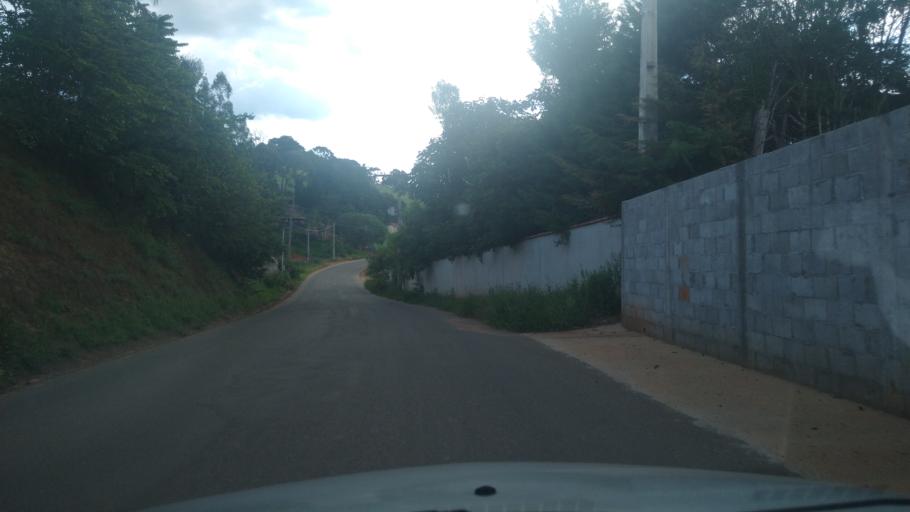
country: BR
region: Minas Gerais
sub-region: Extrema
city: Extrema
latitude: -22.7215
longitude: -46.3439
